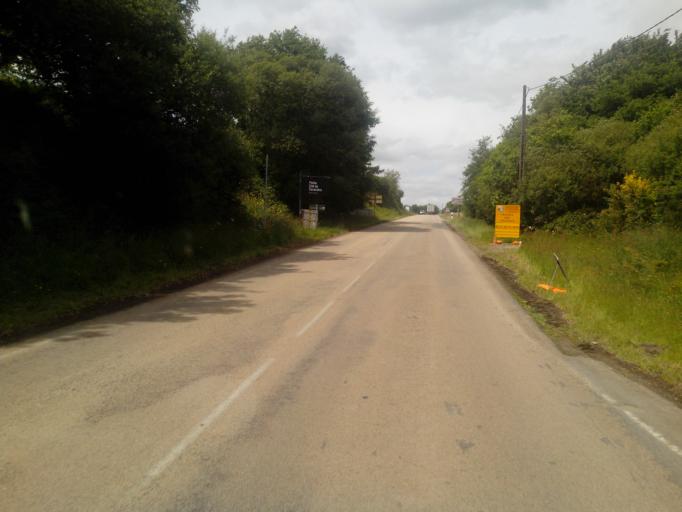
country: FR
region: Brittany
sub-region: Departement du Finistere
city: Guerlesquin
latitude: 48.5214
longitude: -3.5910
